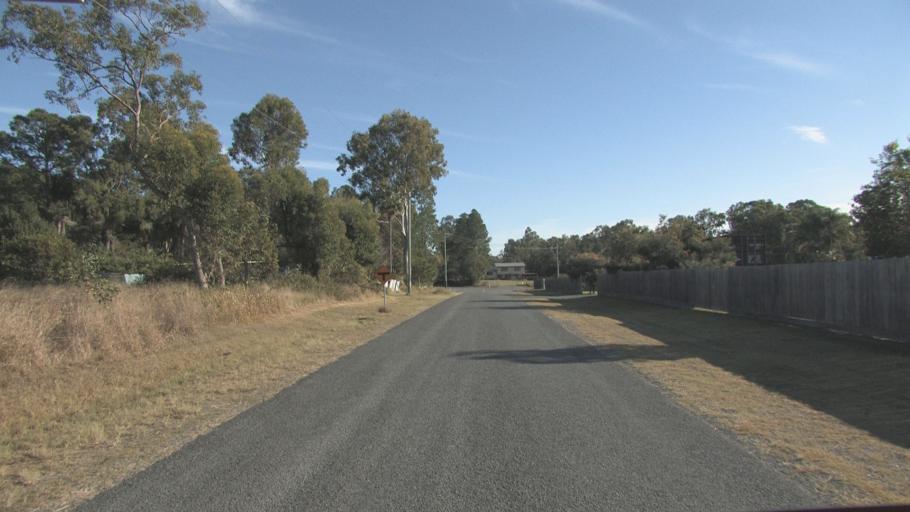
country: AU
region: Queensland
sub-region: Logan
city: Park Ridge South
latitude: -27.7192
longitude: 152.9710
